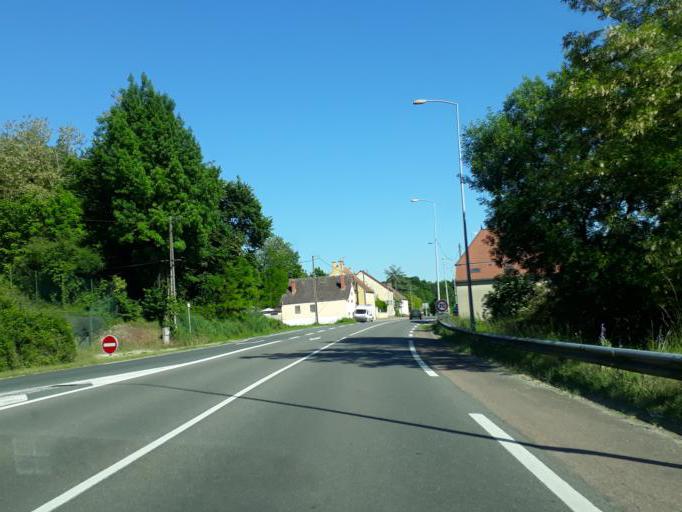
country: FR
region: Bourgogne
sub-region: Departement de la Nievre
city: Neuvy-sur-Loire
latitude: 47.5140
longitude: 2.8892
